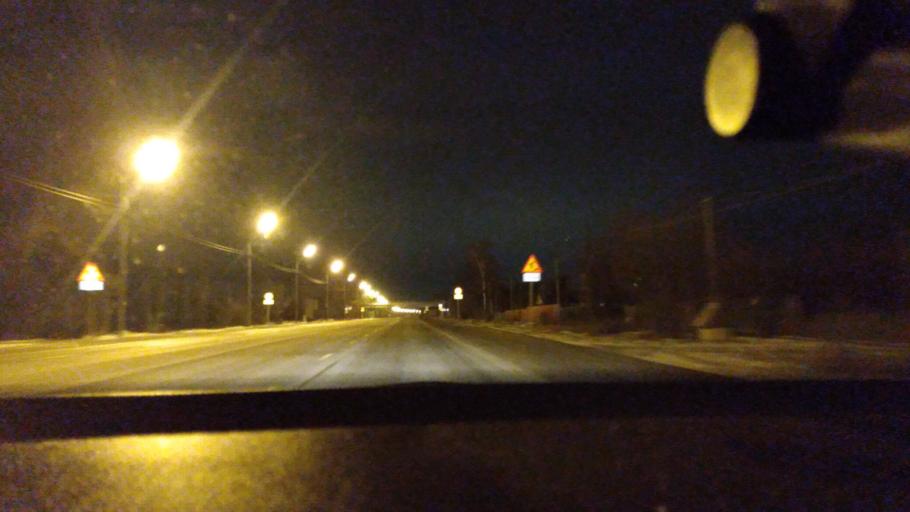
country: RU
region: Moskovskaya
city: Bronnitsy
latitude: 55.3869
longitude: 38.3437
